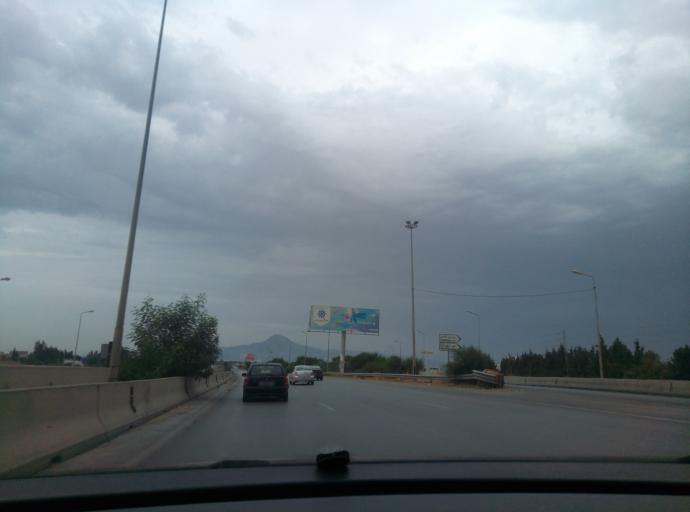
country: TN
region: Bin 'Arus
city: Ben Arous
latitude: 36.7297
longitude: 10.2372
